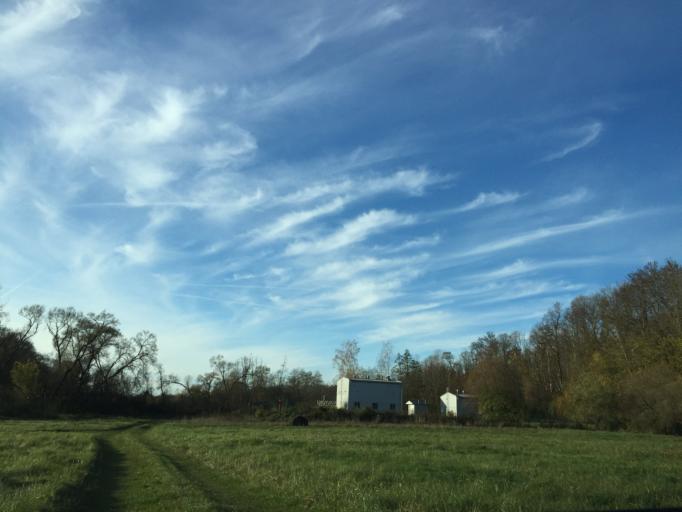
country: LV
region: Skriveri
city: Skriveri
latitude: 56.6220
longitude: 25.1253
